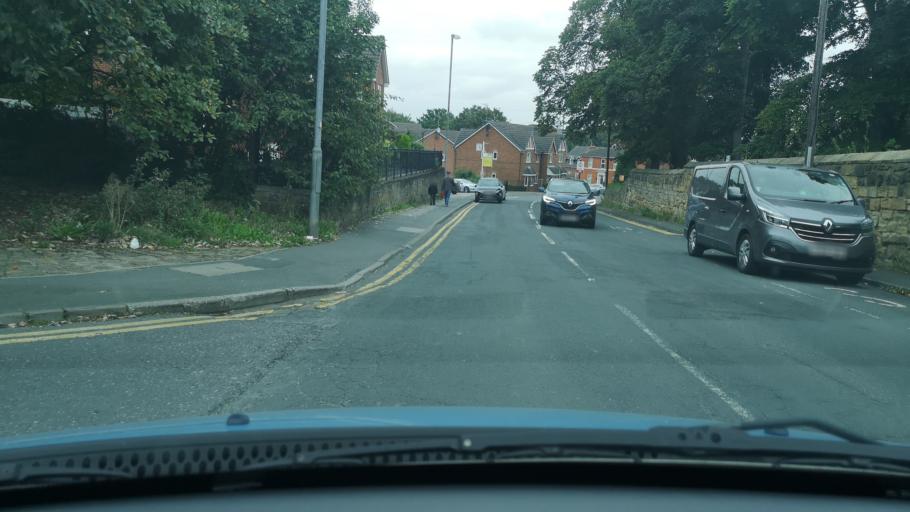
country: GB
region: England
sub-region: City and Borough of Wakefield
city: Pontefract
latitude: 53.6956
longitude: -1.3058
